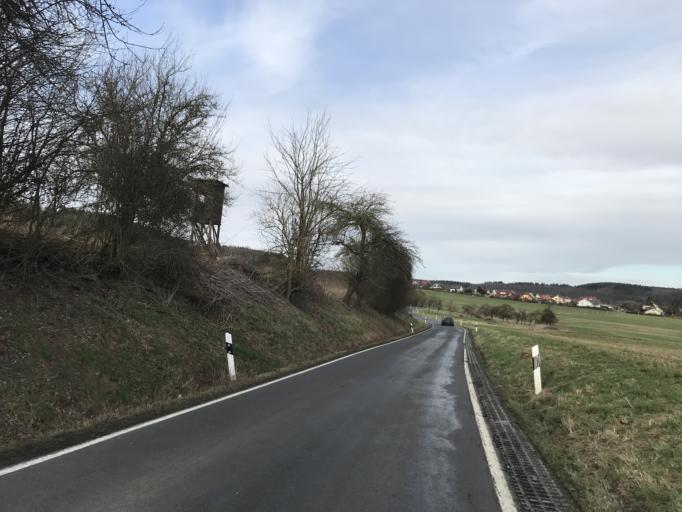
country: DE
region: Hesse
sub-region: Regierungsbezirk Giessen
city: Heuchelheim
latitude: 50.6350
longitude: 8.5866
